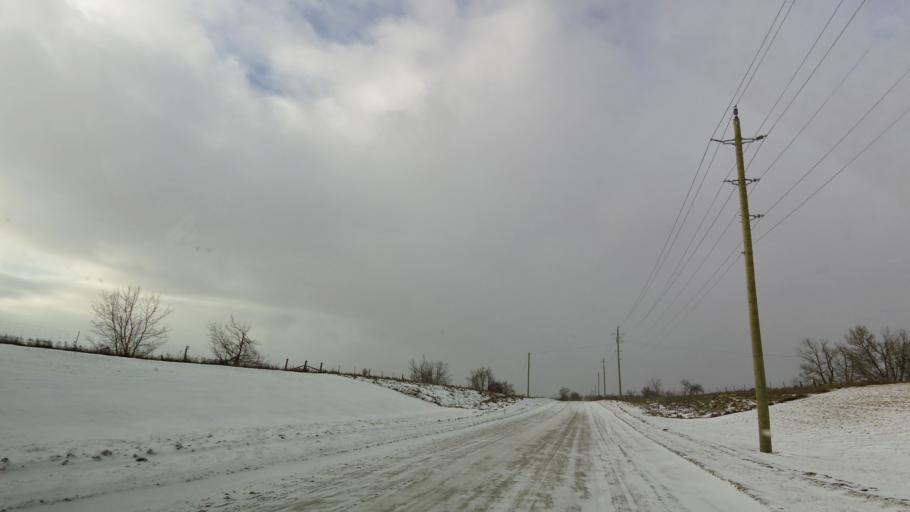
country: CA
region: Ontario
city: Orangeville
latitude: 43.8440
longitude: -79.9977
